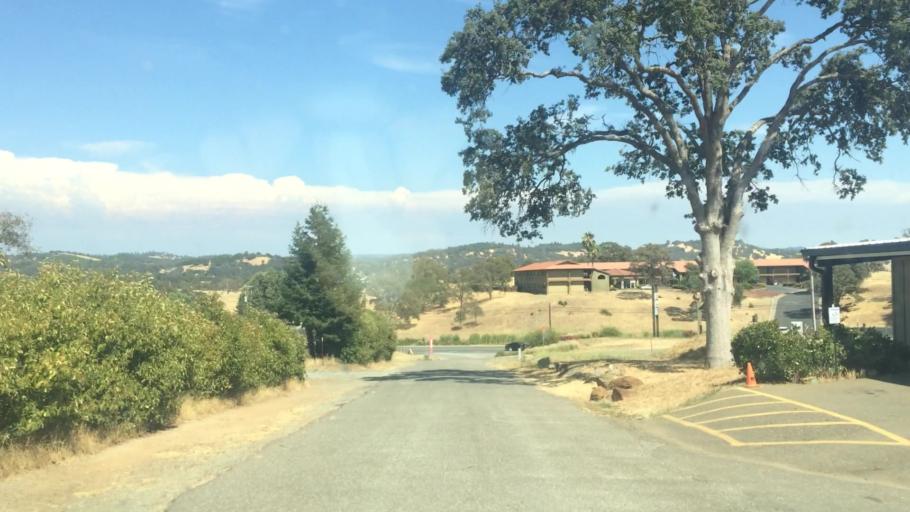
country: US
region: California
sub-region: Amador County
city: Plymouth
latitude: 38.4674
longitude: -120.8565
